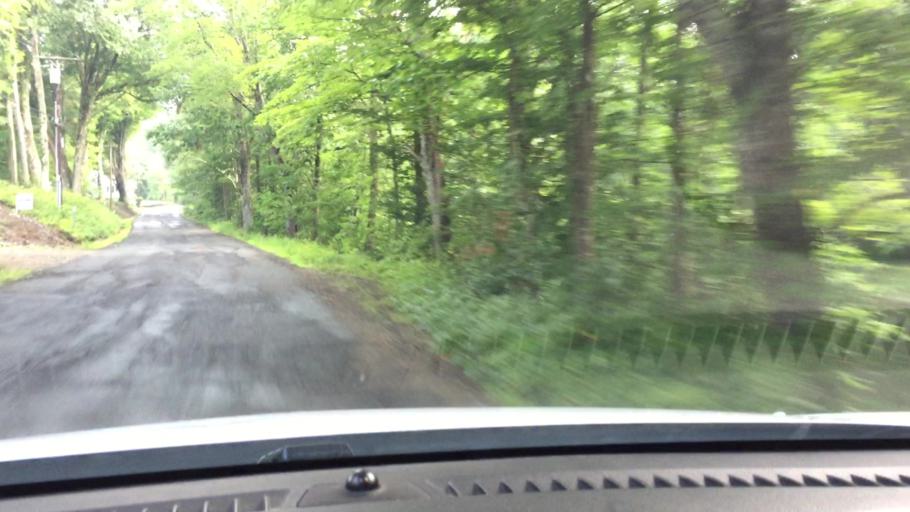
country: US
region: Massachusetts
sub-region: Hampshire County
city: Chesterfield
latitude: 42.3040
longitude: -72.9078
